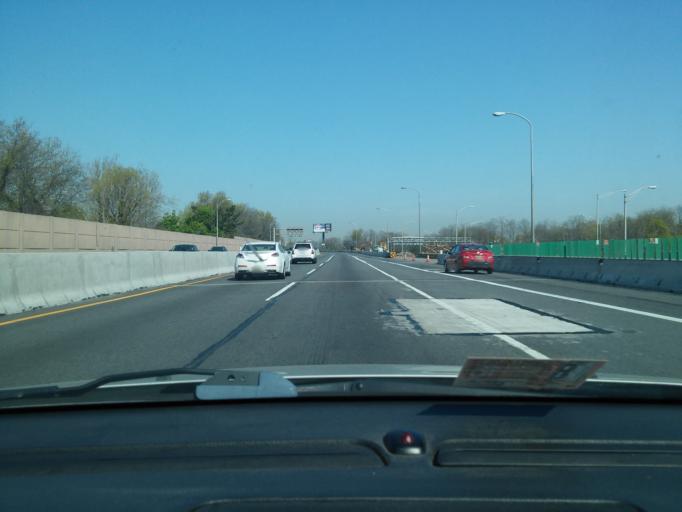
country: US
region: New Jersey
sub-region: Hudson County
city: Bayonne
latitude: 40.6886
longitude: -74.1006
